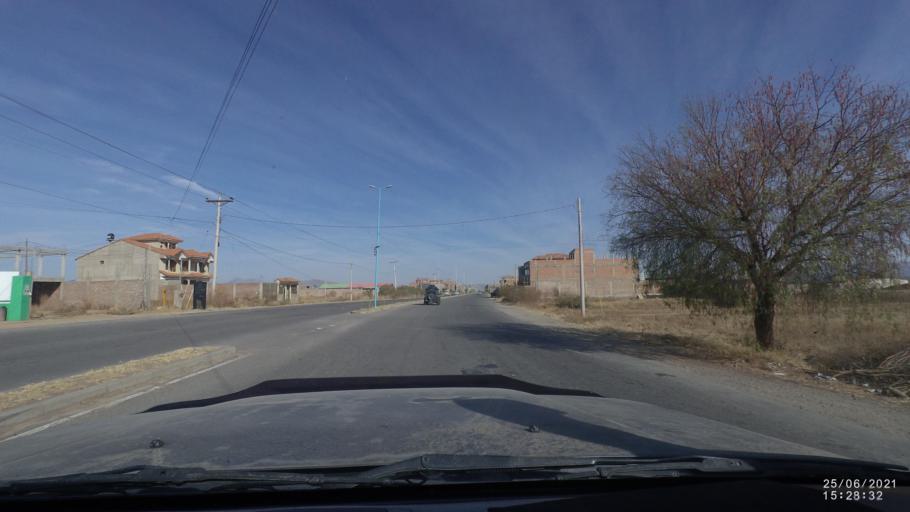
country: BO
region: Cochabamba
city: Cliza
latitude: -17.5604
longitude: -65.9367
